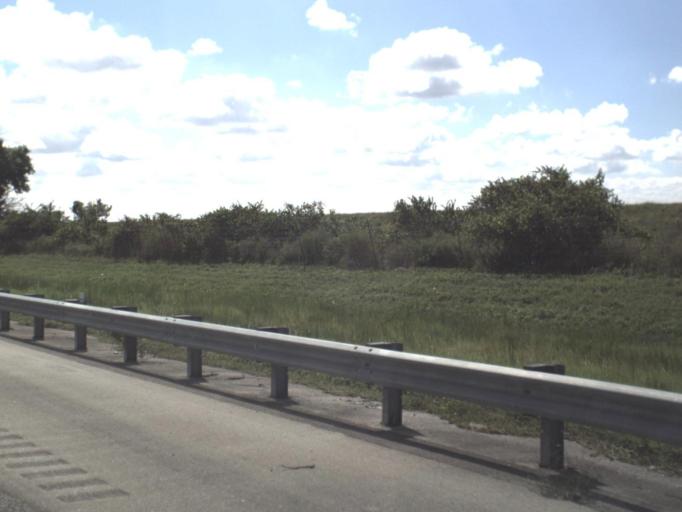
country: US
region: Florida
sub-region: Broward County
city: Coral Springs
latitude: 26.2547
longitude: -80.2974
